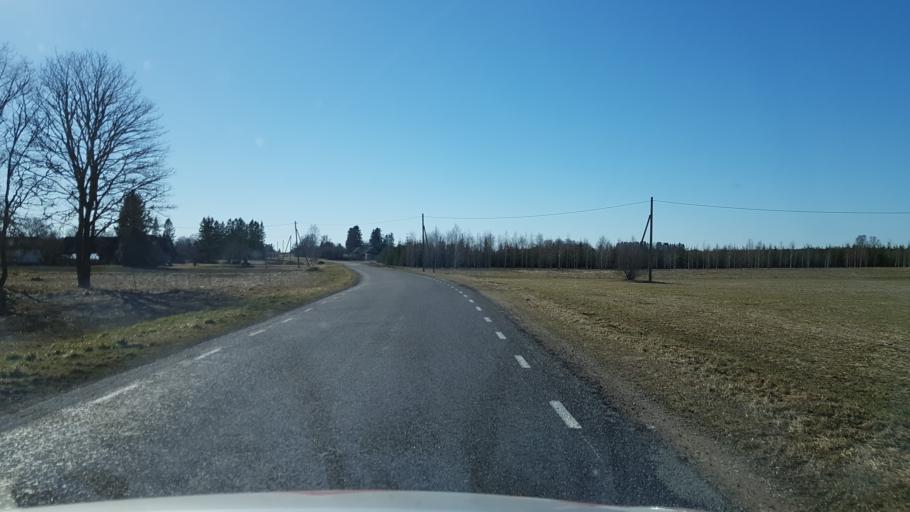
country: EE
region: Laeaene-Virumaa
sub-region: Haljala vald
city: Haljala
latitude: 59.4360
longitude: 26.1976
